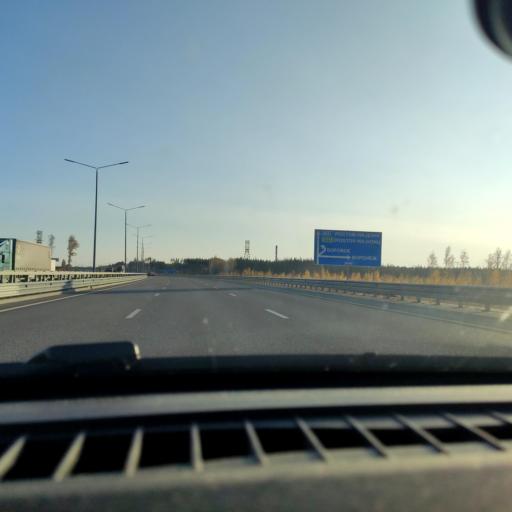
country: RU
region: Voronezj
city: Somovo
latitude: 51.7490
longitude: 39.3054
